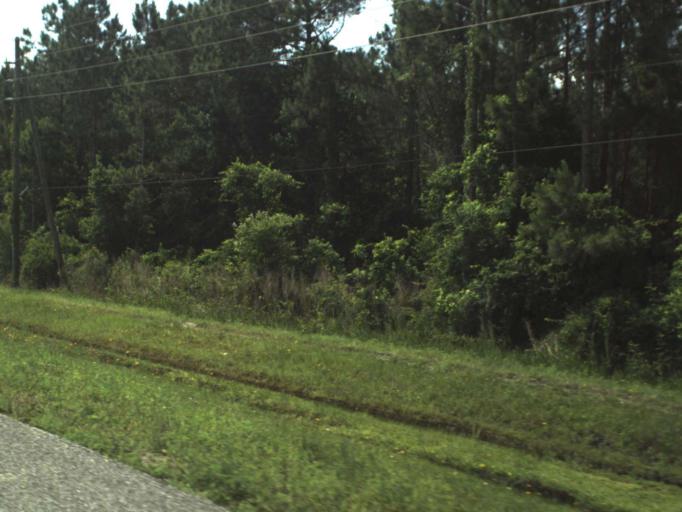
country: US
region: Florida
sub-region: Volusia County
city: Samsula-Spruce Creek
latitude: 29.0240
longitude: -81.1206
